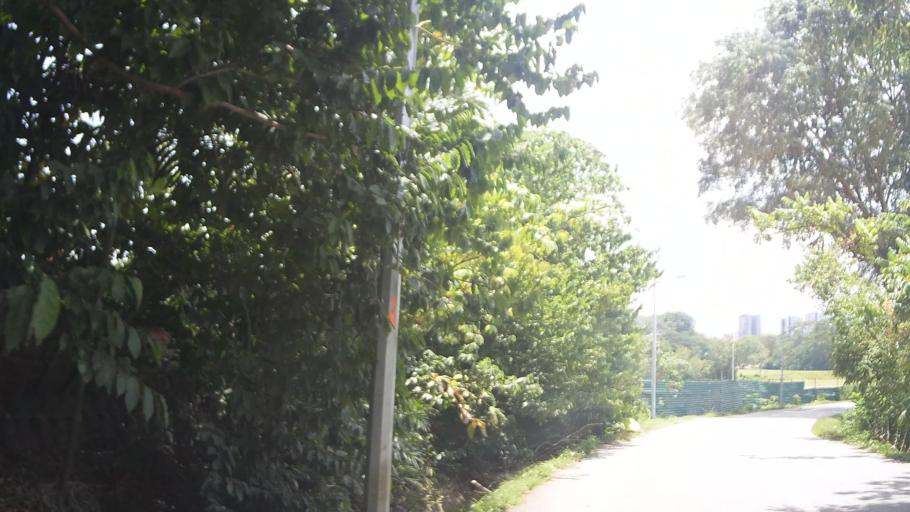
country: MY
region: Johor
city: Kampung Pasir Gudang Baru
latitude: 1.3959
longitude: 103.8648
